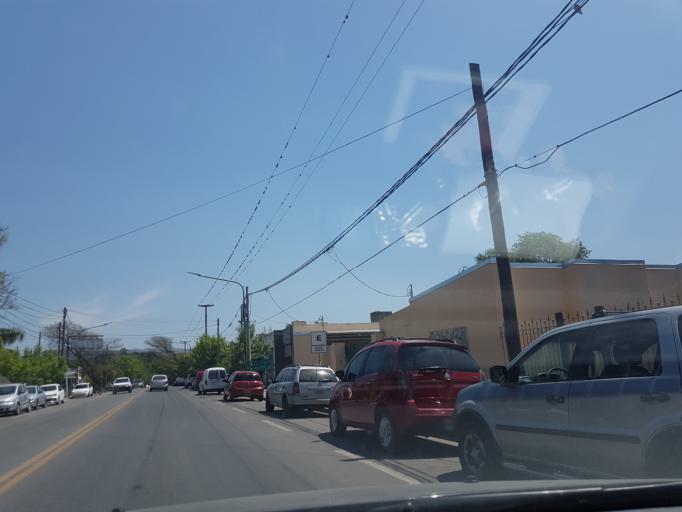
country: AR
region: Cordoba
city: Villa Allende
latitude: -31.2948
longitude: -64.2988
